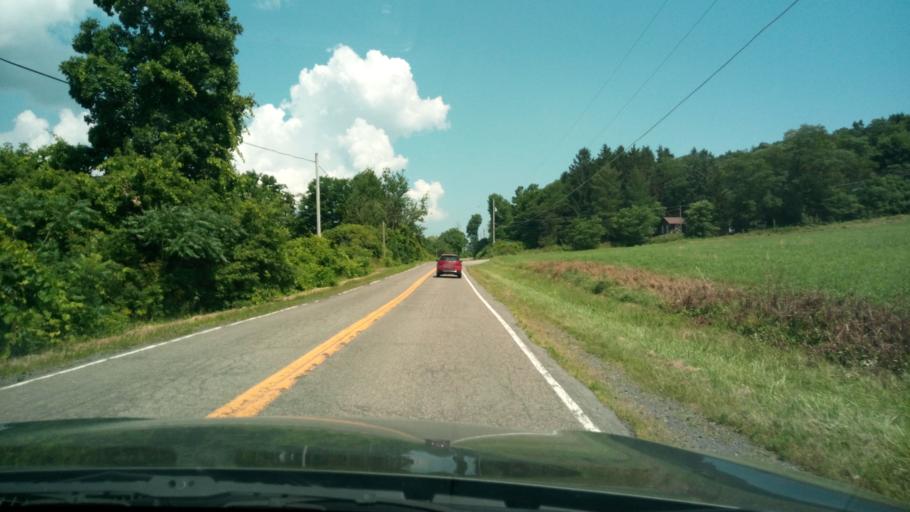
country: US
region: New York
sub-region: Chemung County
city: Horseheads North
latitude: 42.2590
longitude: -76.8014
